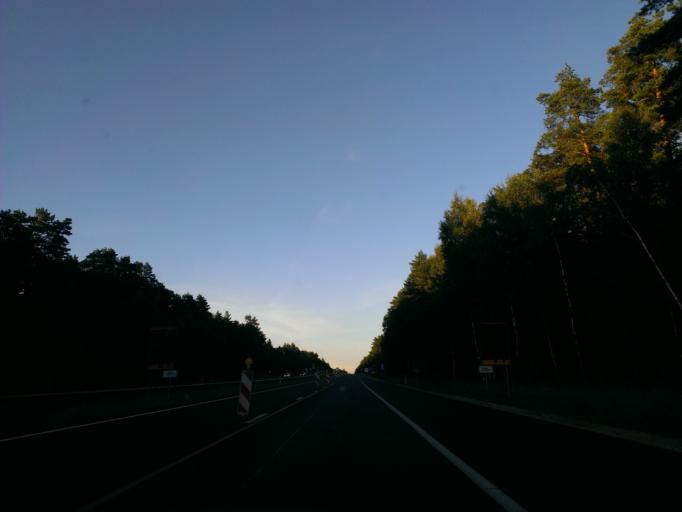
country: LV
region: Riga
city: Bergi
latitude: 57.0140
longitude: 24.3206
